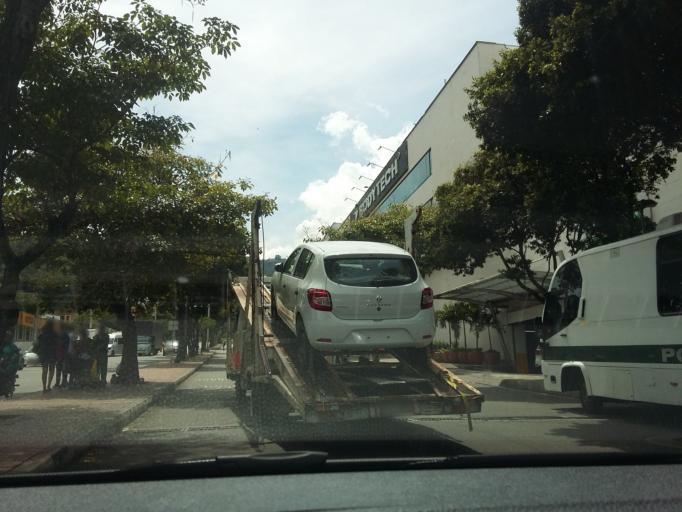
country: CO
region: Santander
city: Bucaramanga
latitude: 7.1310
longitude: -73.1127
